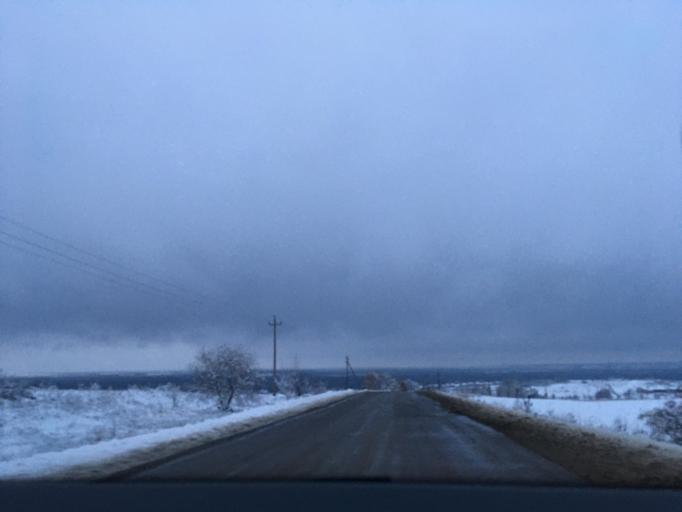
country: RU
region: Voronezj
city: Verkhniy Mamon
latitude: 50.0713
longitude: 40.2884
